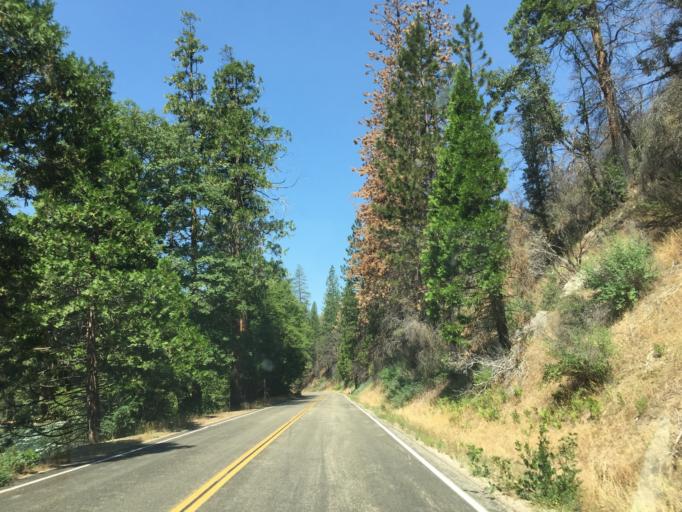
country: US
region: California
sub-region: Tulare County
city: Three Rivers
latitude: 36.8040
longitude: -118.7106
